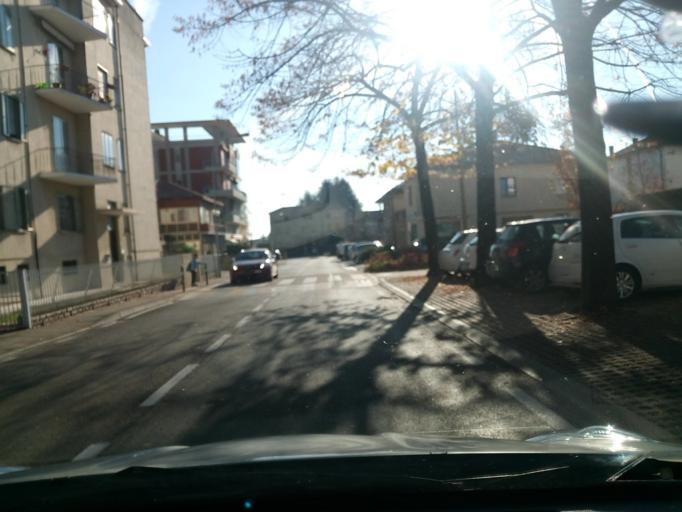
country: IT
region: Veneto
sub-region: Provincia di Vicenza
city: Schio
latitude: 45.7138
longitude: 11.3689
